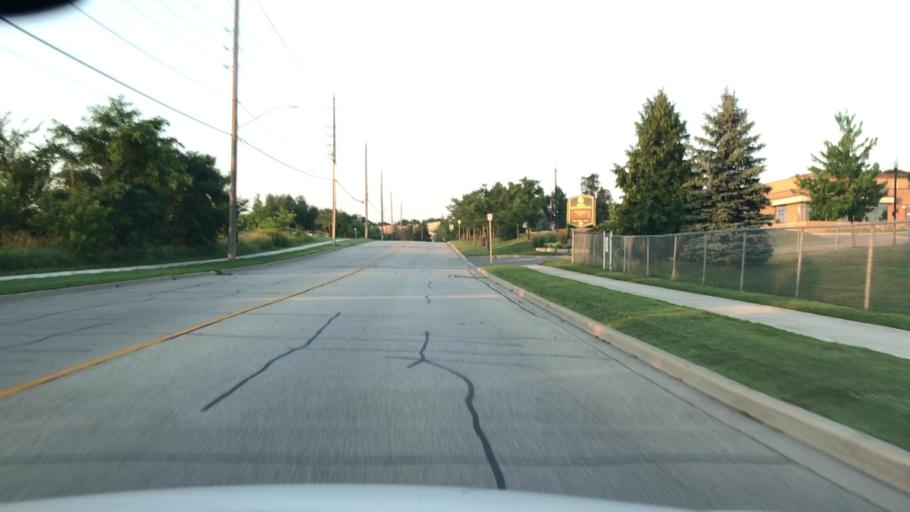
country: CA
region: Ontario
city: Newmarket
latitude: 44.0186
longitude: -79.4620
